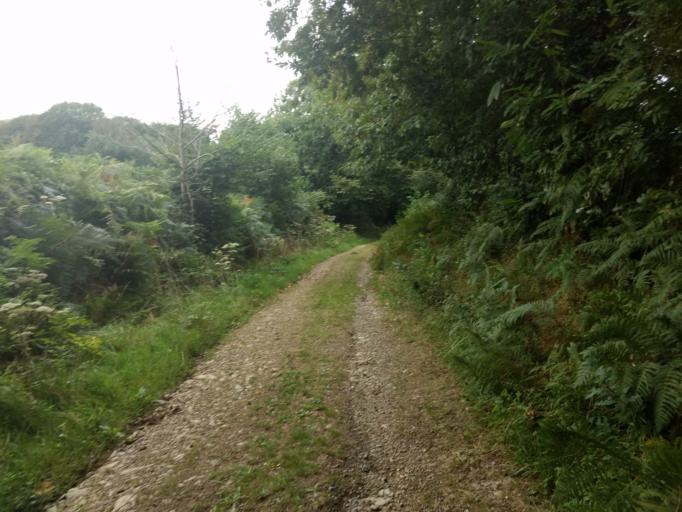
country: FR
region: Brittany
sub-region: Departement du Finistere
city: Loperhet
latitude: 48.3721
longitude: -4.2939
